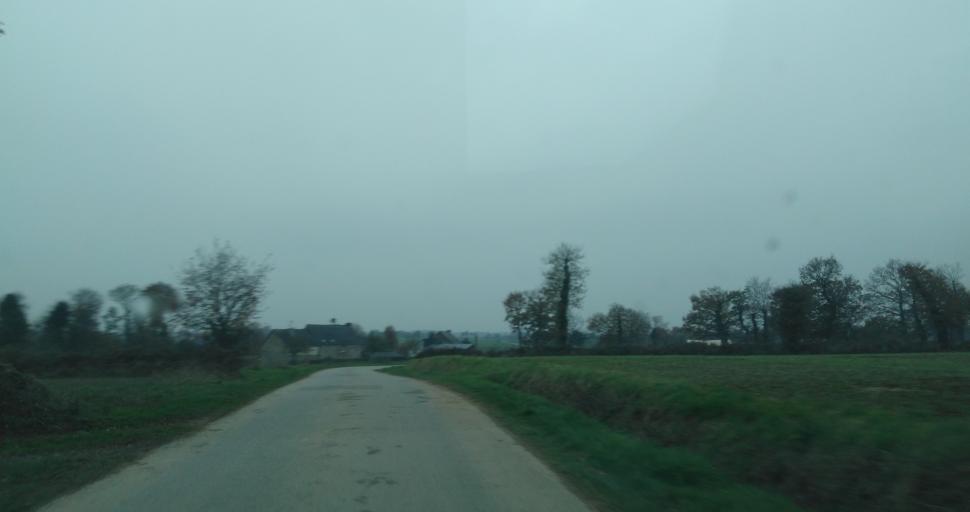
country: FR
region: Brittany
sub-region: Departement d'Ille-et-Vilaine
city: Iffendic
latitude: 48.0960
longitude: -2.0751
